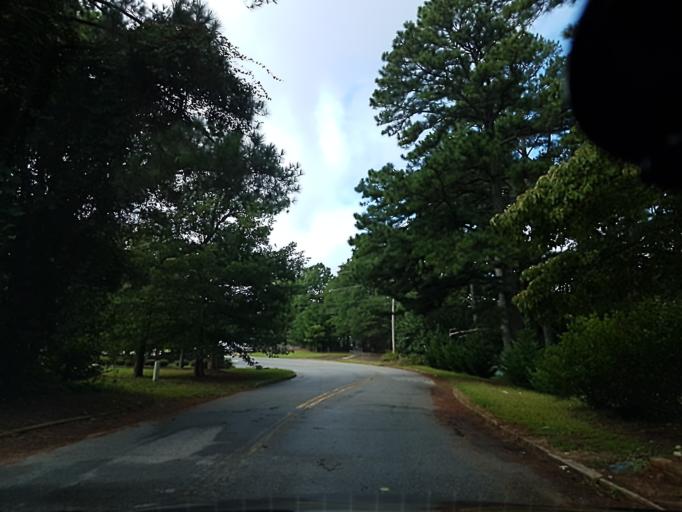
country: US
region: Georgia
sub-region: Fulton County
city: Fairburn
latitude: 33.5797
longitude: -84.5787
